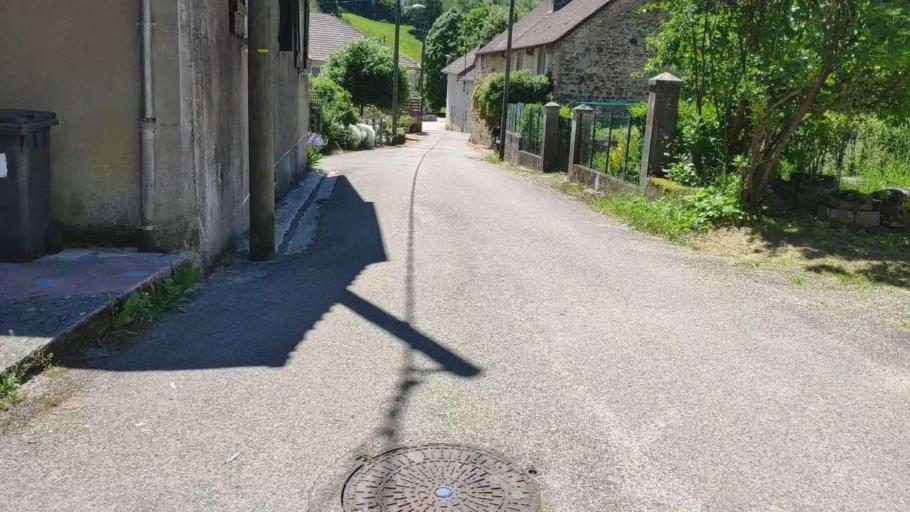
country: FR
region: Franche-Comte
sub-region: Departement du Jura
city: Poligny
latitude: 46.7494
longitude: 5.6703
